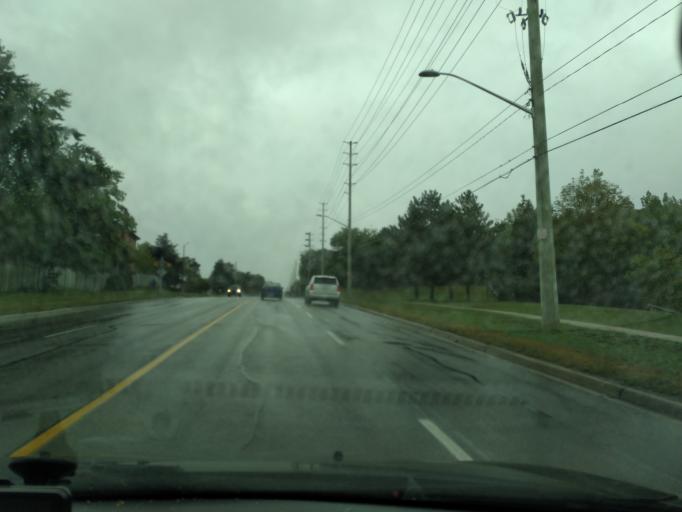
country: CA
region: Ontario
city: Barrie
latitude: 44.3881
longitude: -79.7100
